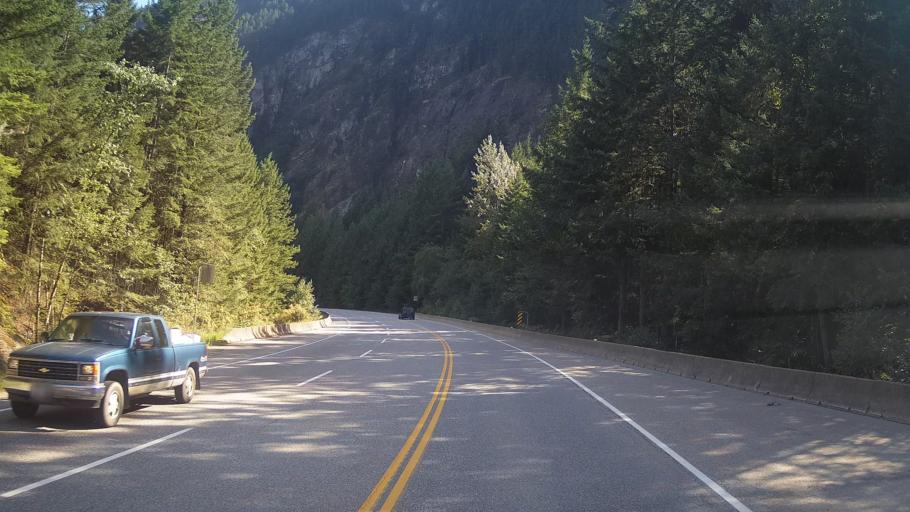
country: CA
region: British Columbia
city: Hope
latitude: 49.6463
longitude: -121.4111
